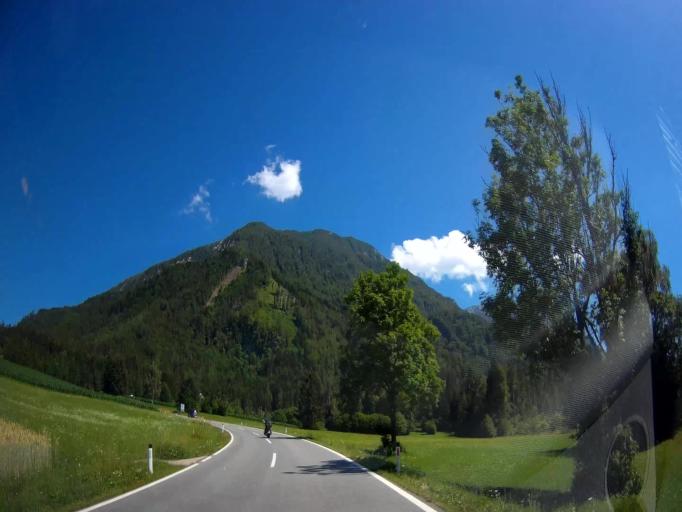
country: AT
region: Carinthia
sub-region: Politischer Bezirk Volkermarkt
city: Gallizien
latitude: 46.5336
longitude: 14.4584
